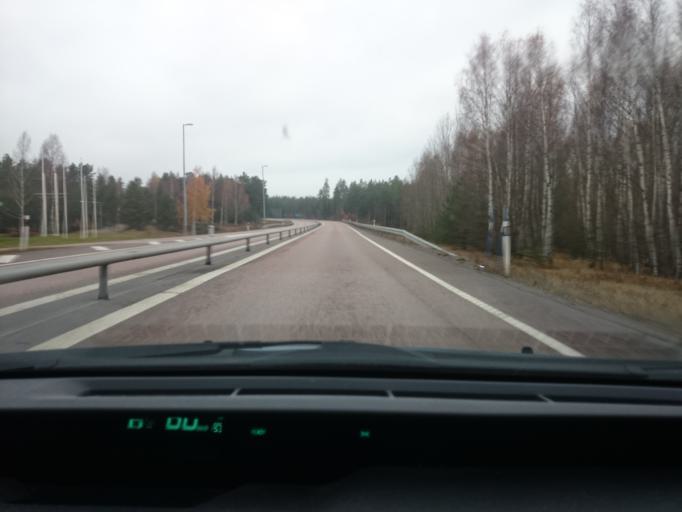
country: SE
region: Dalarna
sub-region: Avesta Kommun
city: Avesta
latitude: 60.1533
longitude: 16.2008
